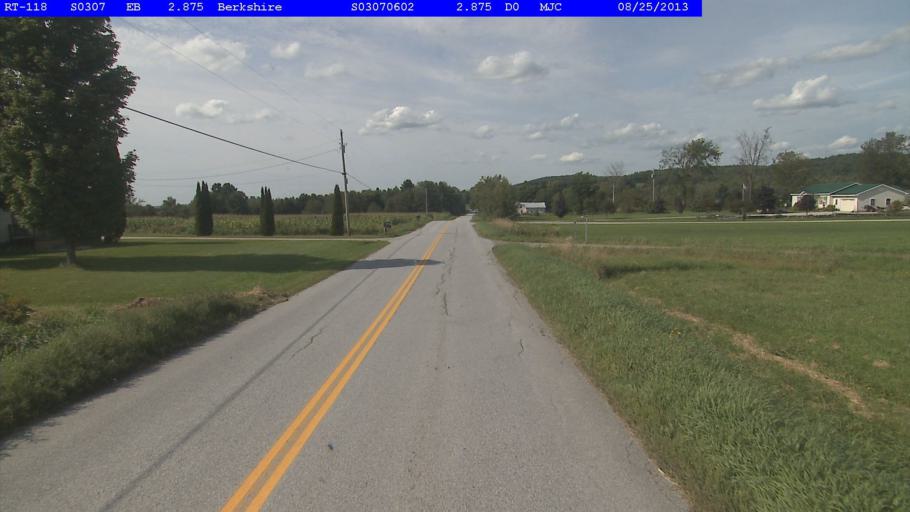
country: US
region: Vermont
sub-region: Franklin County
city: Enosburg Falls
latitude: 44.9573
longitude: -72.7554
